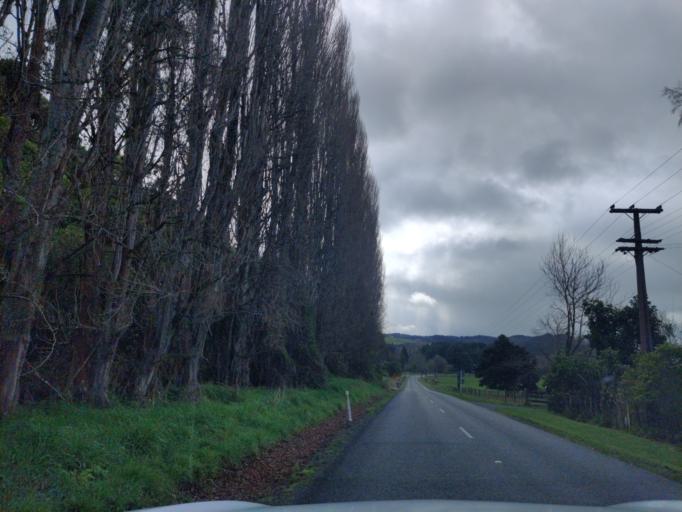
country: NZ
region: Manawatu-Wanganui
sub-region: Palmerston North City
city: Palmerston North
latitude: -40.1803
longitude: 175.7887
